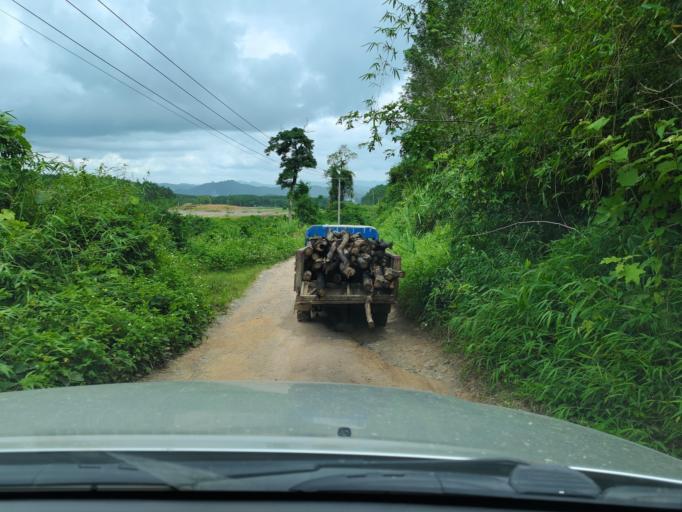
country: LA
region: Loungnamtha
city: Muang Long
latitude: 20.7006
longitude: 101.0351
